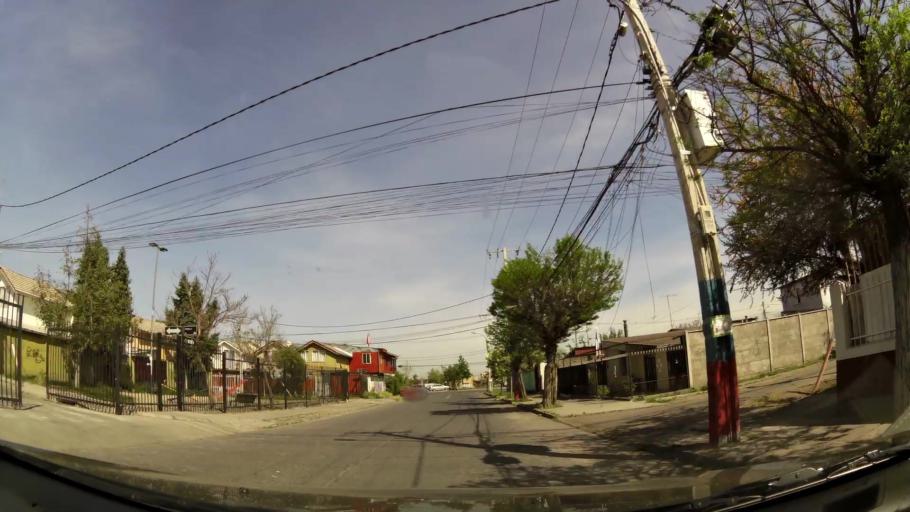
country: CL
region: Santiago Metropolitan
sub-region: Provincia de Cordillera
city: Puente Alto
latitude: -33.6115
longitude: -70.5867
